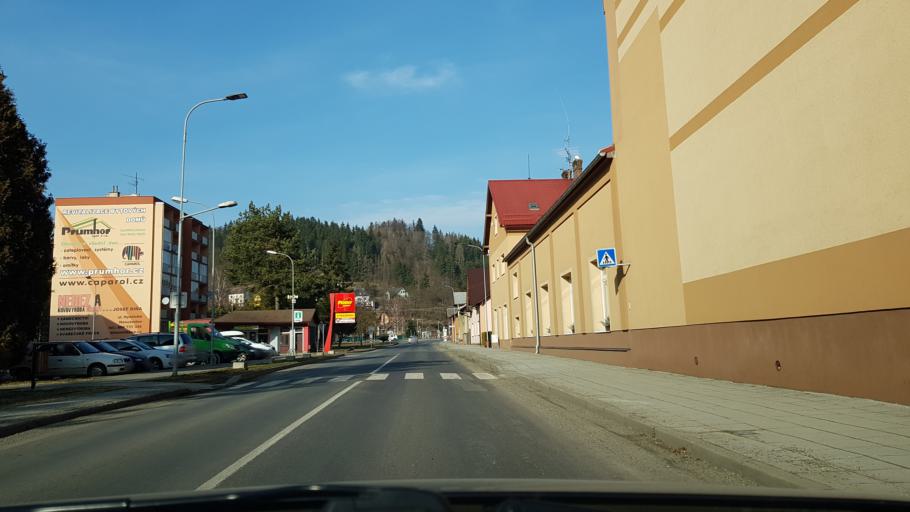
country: CZ
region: Olomoucky
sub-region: Okres Sumperk
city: Hanusovice
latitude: 50.0759
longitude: 16.9323
